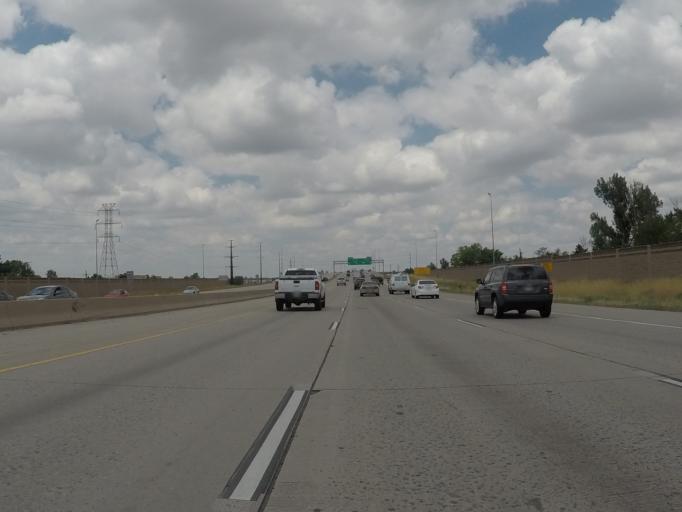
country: US
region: Colorado
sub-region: Adams County
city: Aurora
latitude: 39.7595
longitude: -104.8277
